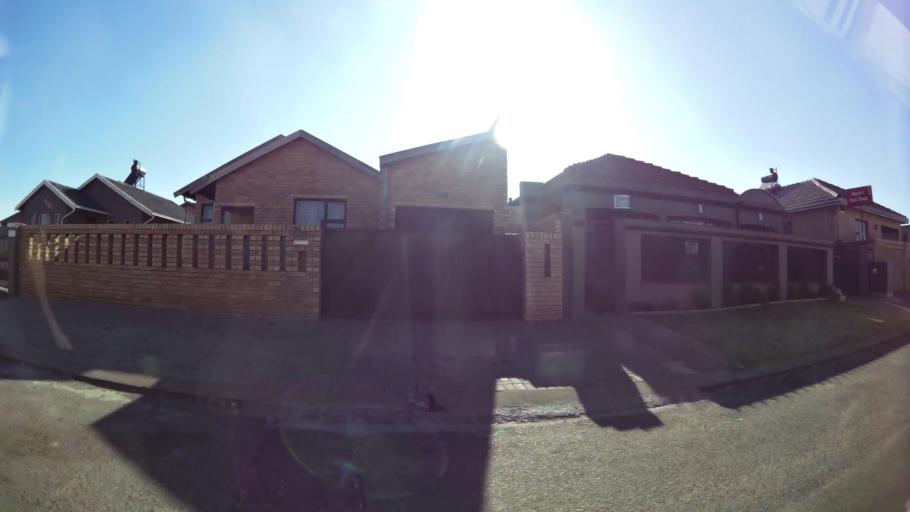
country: ZA
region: Gauteng
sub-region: City of Johannesburg Metropolitan Municipality
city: Soweto
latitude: -26.2312
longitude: 27.9161
